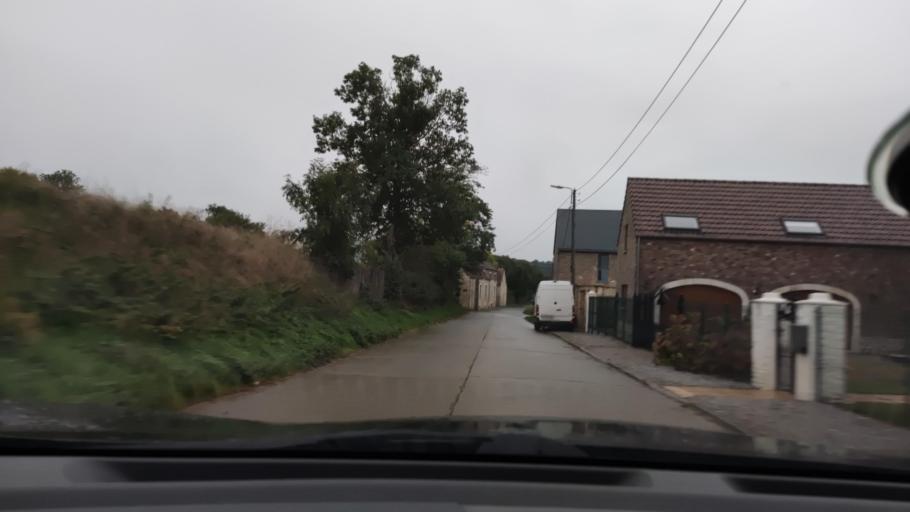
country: BE
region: Wallonia
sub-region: Province du Brabant Wallon
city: Beauvechain
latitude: 50.7616
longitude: 4.8179
